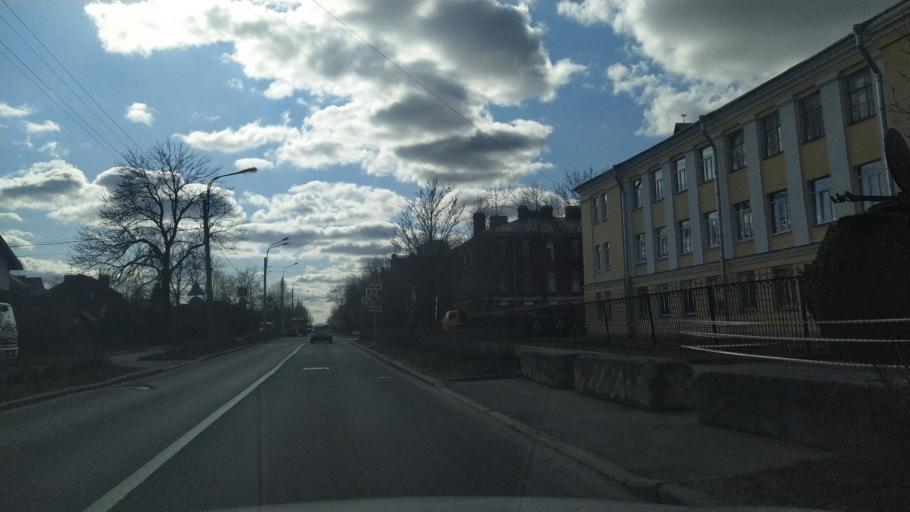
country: RU
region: St.-Petersburg
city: Pushkin
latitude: 59.7039
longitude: 30.4129
